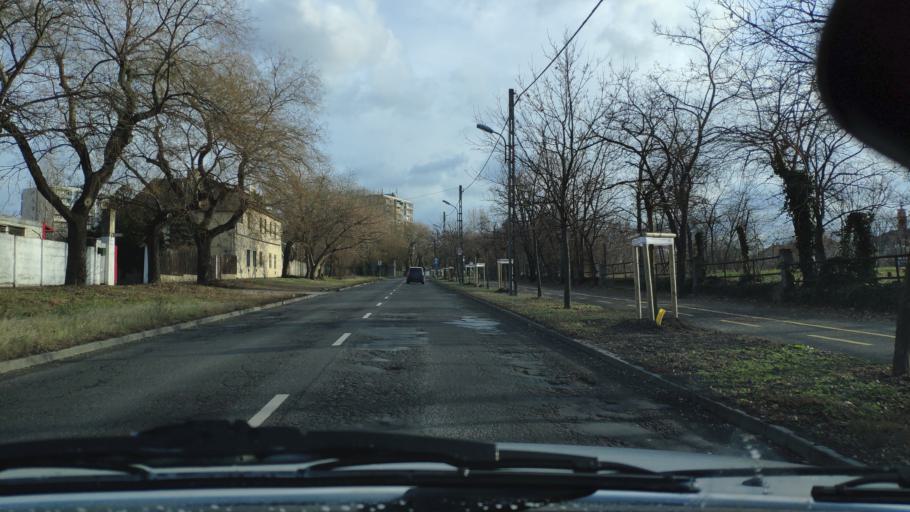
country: HU
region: Budapest
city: Budapest X. keruelet
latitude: 47.4873
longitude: 19.1399
